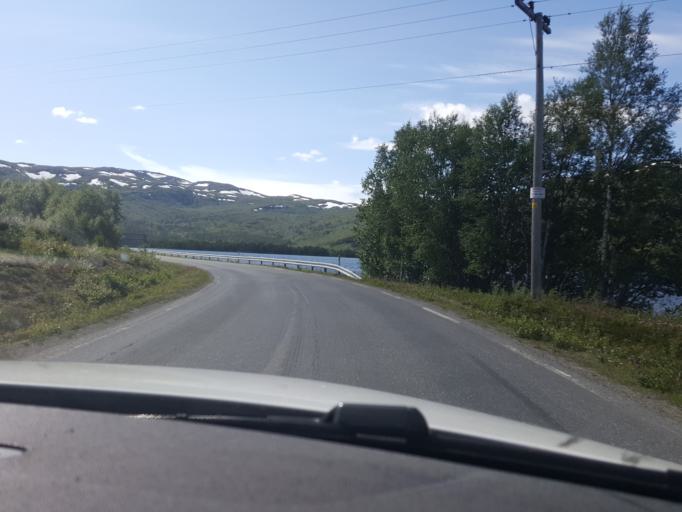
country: NO
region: Nordland
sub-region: Bodo
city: Loding
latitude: 67.0470
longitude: 14.9979
